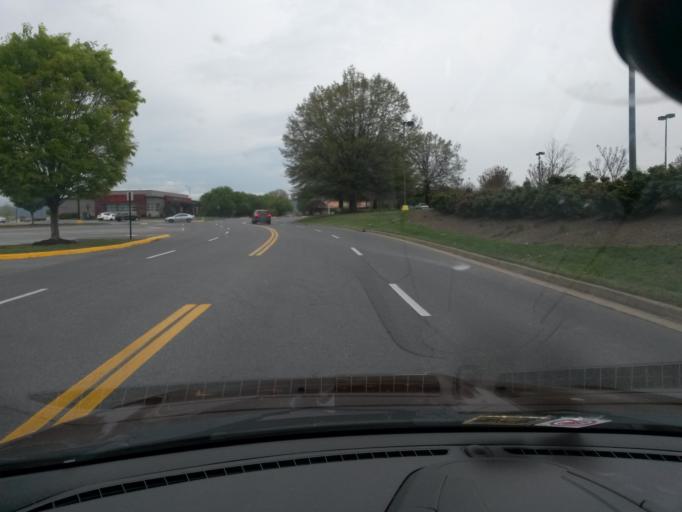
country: US
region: Virginia
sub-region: Roanoke County
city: Hollins
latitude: 37.3061
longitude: -79.9630
